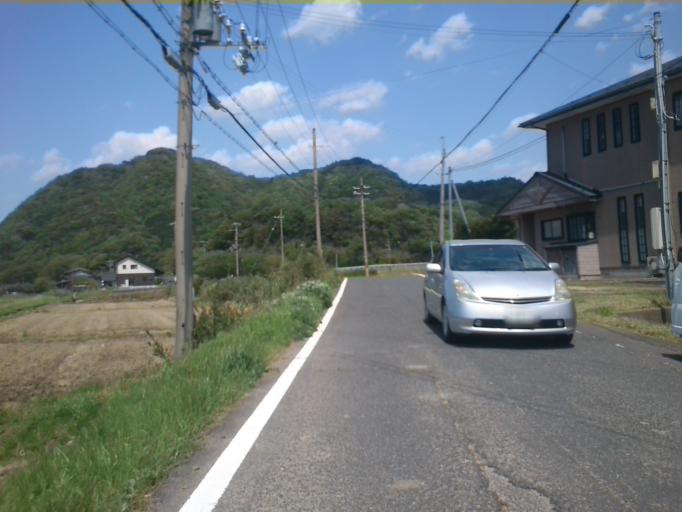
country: JP
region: Kyoto
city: Miyazu
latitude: 35.7334
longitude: 135.1085
